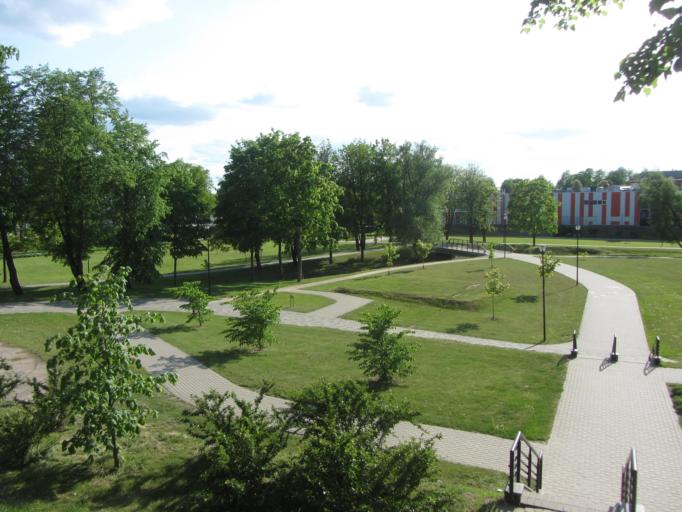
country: LT
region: Utenos apskritis
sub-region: Utena
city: Utena
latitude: 55.4991
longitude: 25.5992
